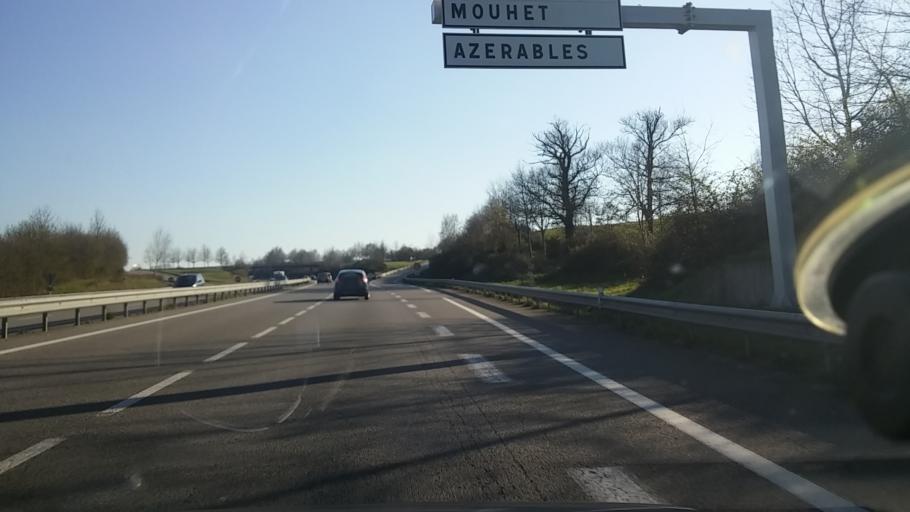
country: FR
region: Limousin
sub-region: Departement de la Haute-Vienne
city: Saint-Sulpice-les-Feuilles
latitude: 46.3582
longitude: 1.4288
